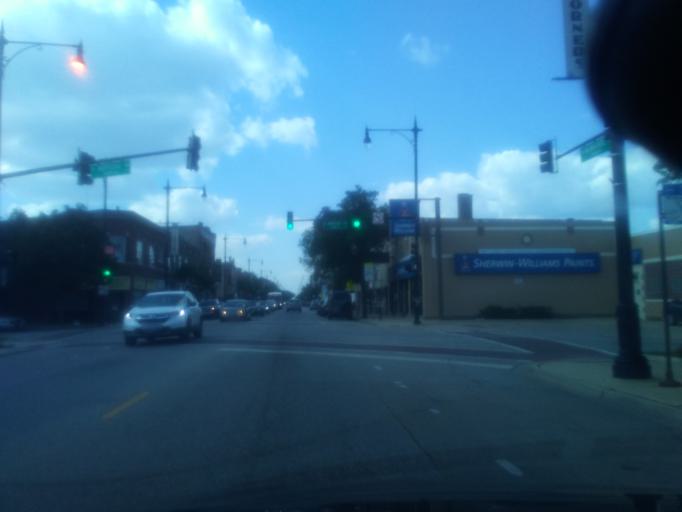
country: US
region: Illinois
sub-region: Cook County
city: Lincolnwood
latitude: 41.9569
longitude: -87.7512
